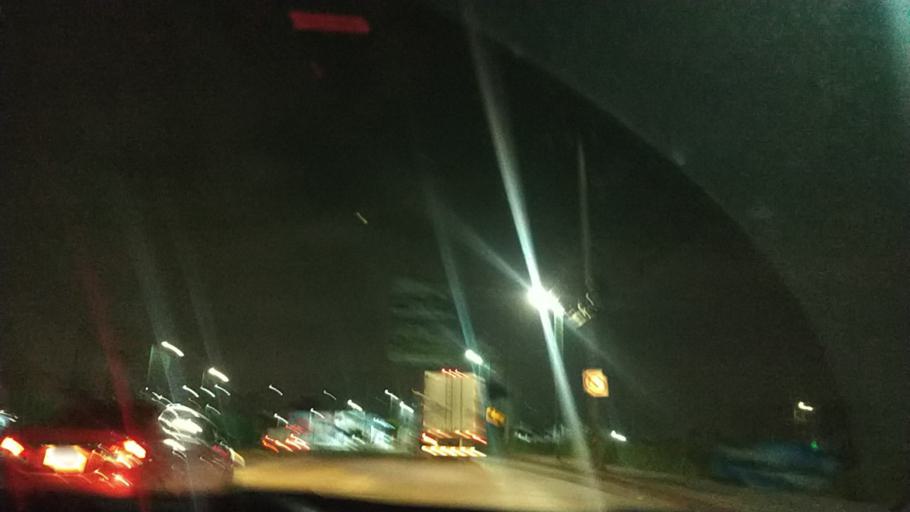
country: MX
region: Mexico
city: Coacalco
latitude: 19.6362
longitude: -99.1089
